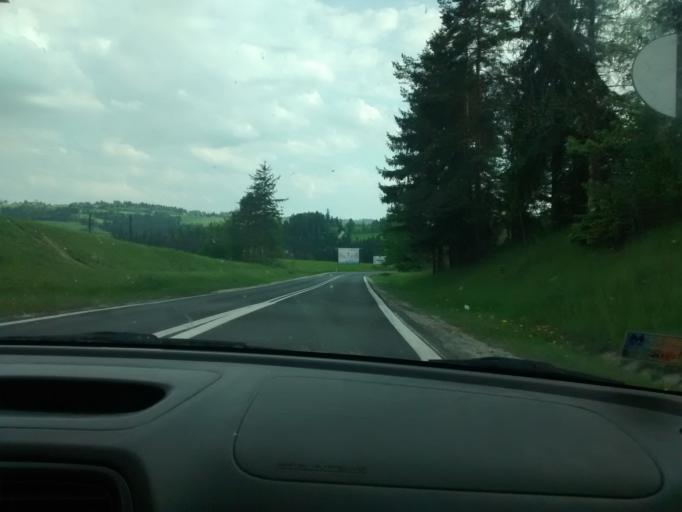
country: PL
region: Lesser Poland Voivodeship
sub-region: Powiat nowotarski
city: Rokiciny
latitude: 49.5718
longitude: 19.9474
